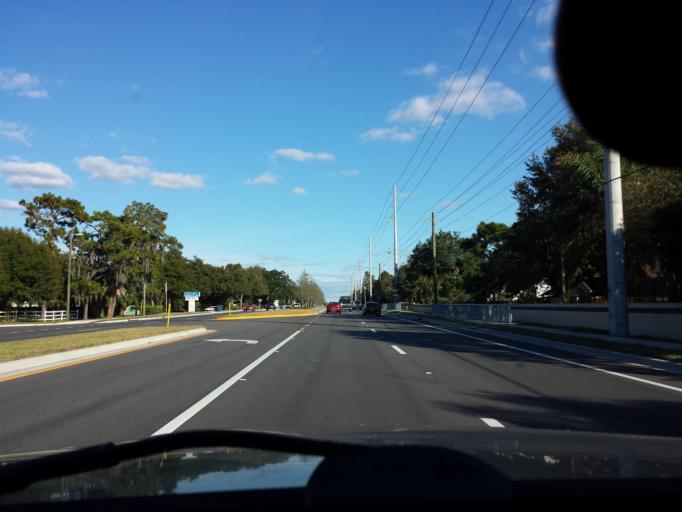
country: US
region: Florida
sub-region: Hillsborough County
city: Riverview
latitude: 27.8535
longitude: -82.2964
